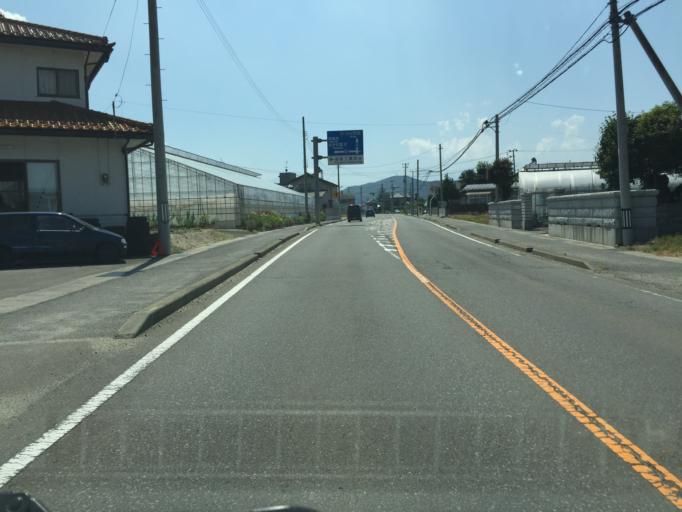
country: JP
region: Fukushima
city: Hobaramachi
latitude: 37.7908
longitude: 140.5123
